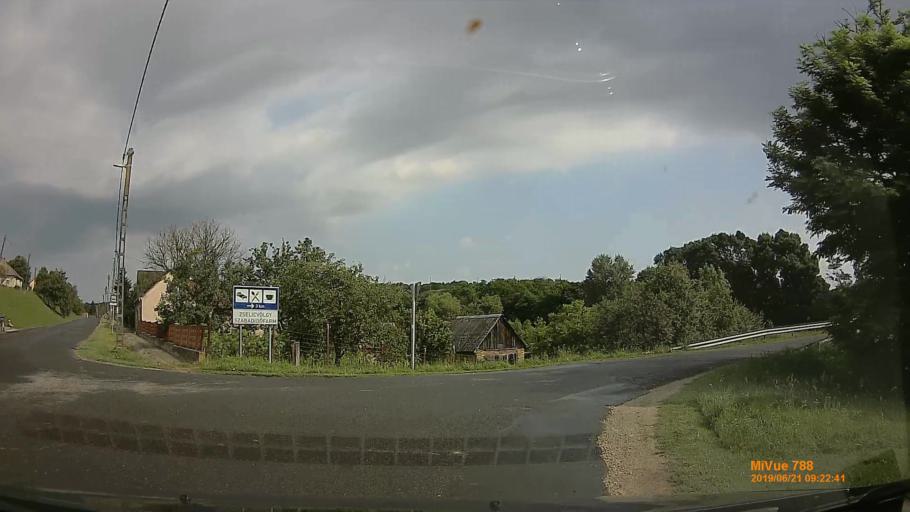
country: HU
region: Somogy
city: Taszar
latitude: 46.2474
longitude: 17.8911
